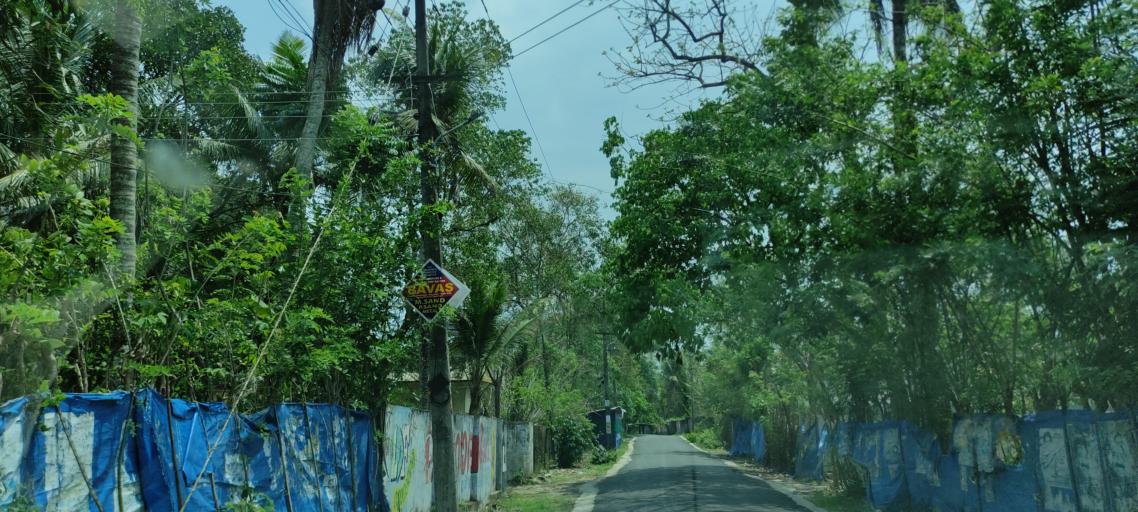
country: IN
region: Kerala
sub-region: Alappuzha
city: Vayalar
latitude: 9.7200
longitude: 76.3408
